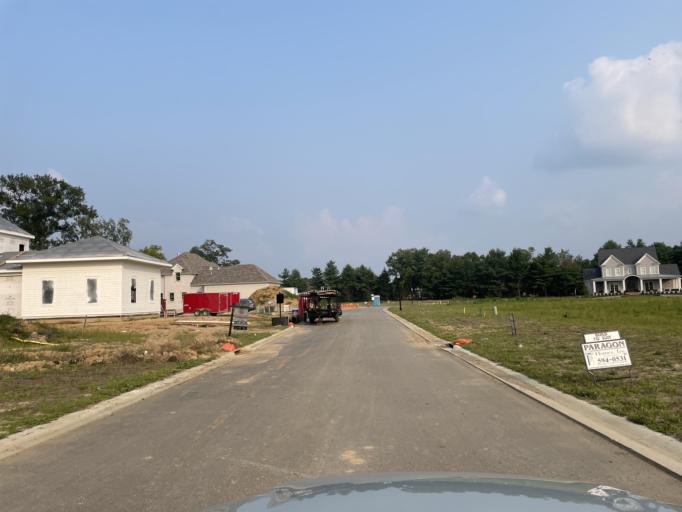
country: US
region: Kentucky
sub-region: Jefferson County
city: Prospect
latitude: 38.3576
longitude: -85.6232
